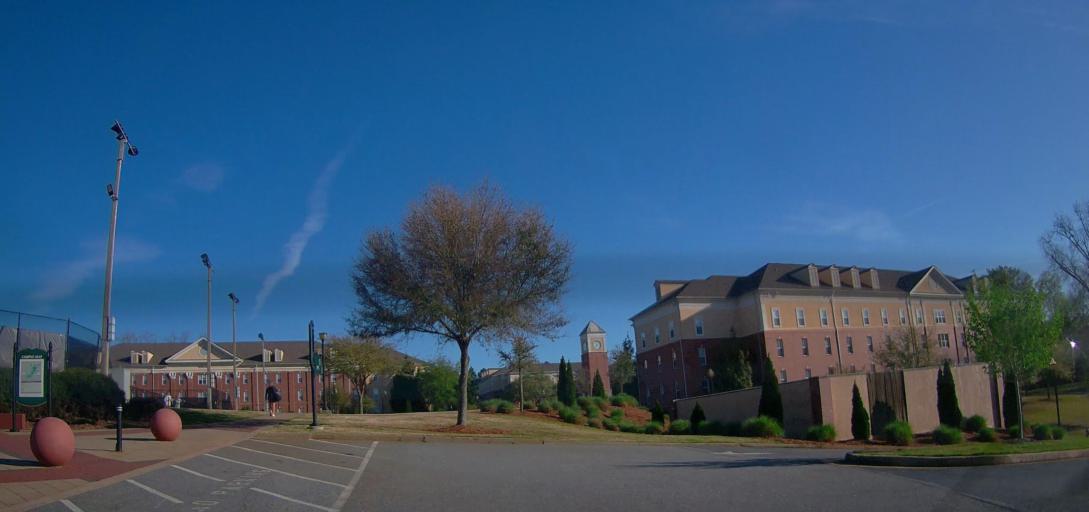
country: US
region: Georgia
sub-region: Baldwin County
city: Milledgeville
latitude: 33.0768
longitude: -83.2334
